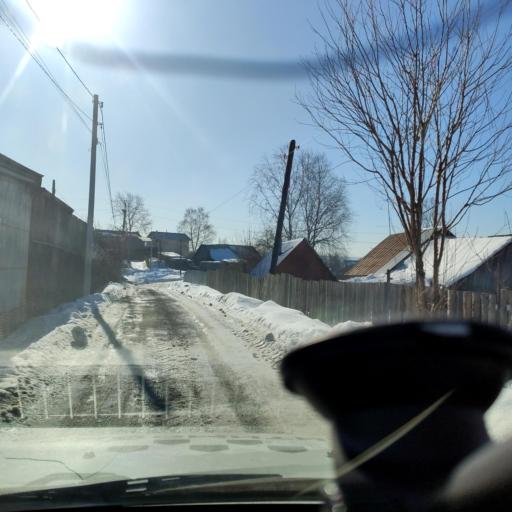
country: RU
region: Perm
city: Ferma
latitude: 57.9381
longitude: 56.3247
